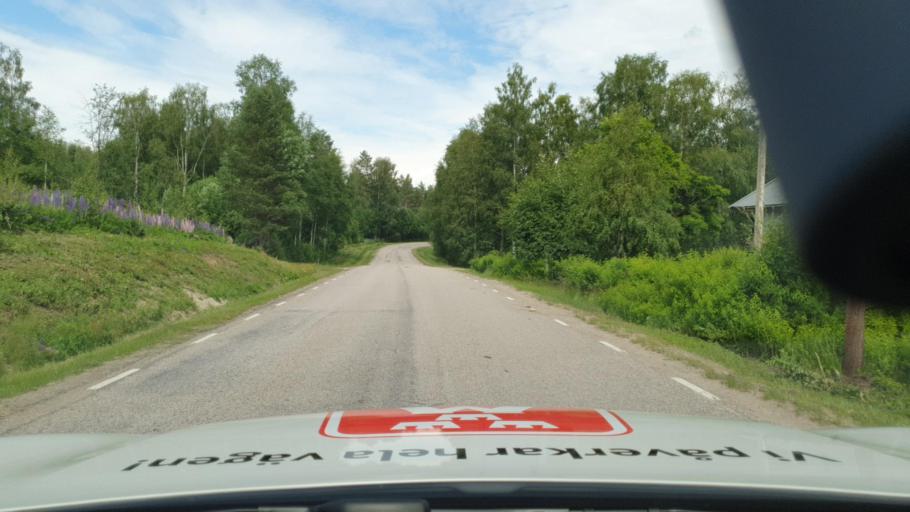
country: NO
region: Hedmark
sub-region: Grue
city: Kirkenaer
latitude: 60.7005
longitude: 12.5882
